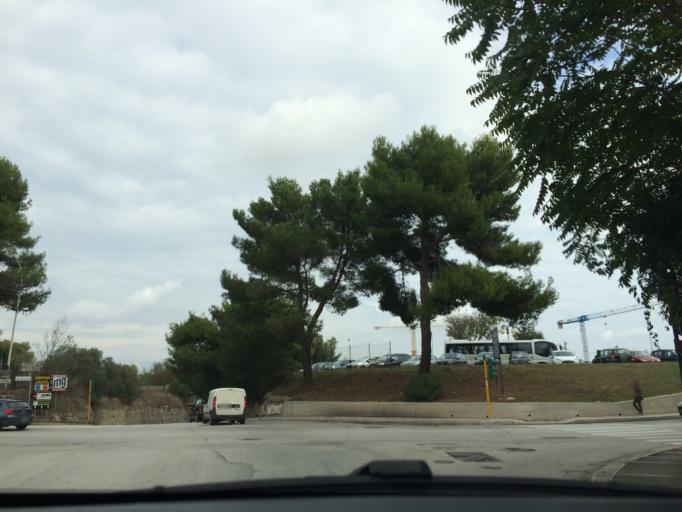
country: IT
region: Basilicate
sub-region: Provincia di Matera
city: Matera
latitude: 40.6793
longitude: 16.5887
